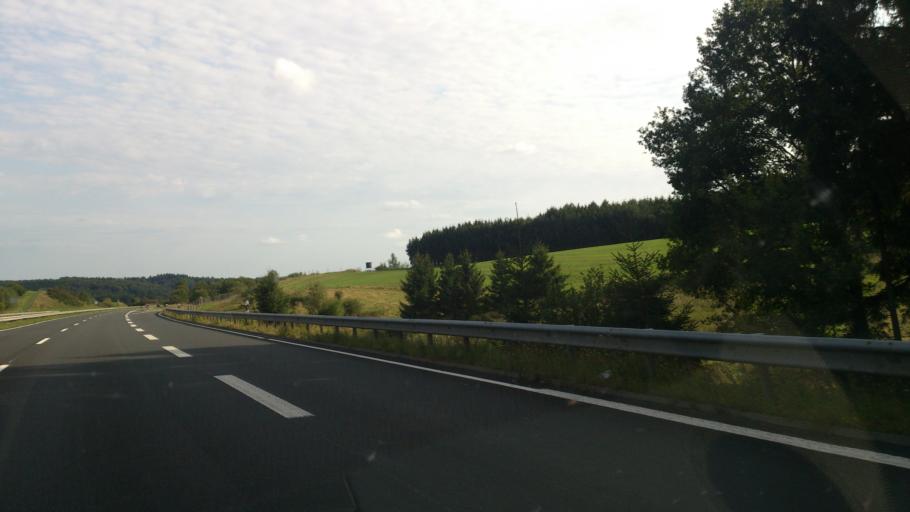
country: DE
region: Rheinland-Pfalz
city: Mehren
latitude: 50.1967
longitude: 6.8943
